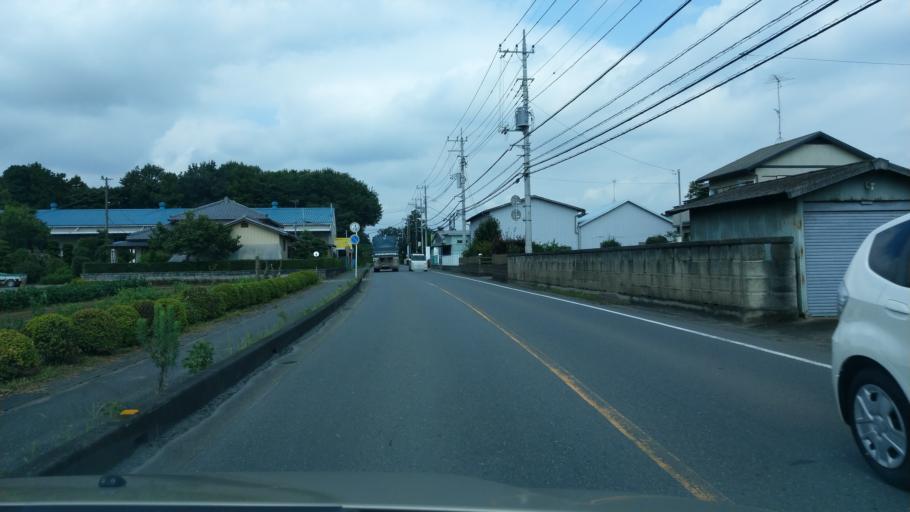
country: JP
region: Saitama
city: Sakado
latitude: 36.0300
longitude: 139.3593
